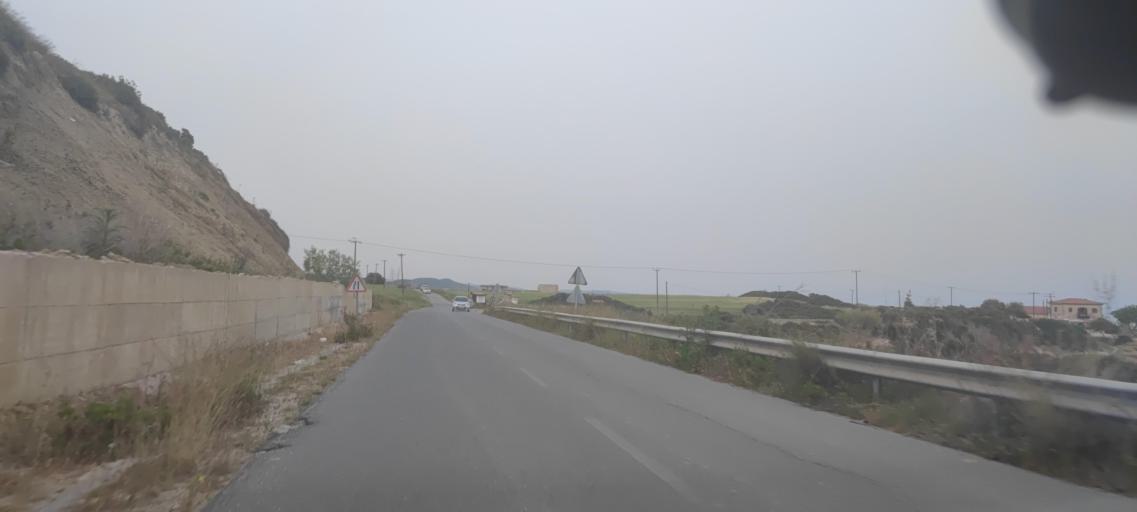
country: CY
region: Ammochostos
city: Rizokarpaso
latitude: 35.5834
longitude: 34.4182
